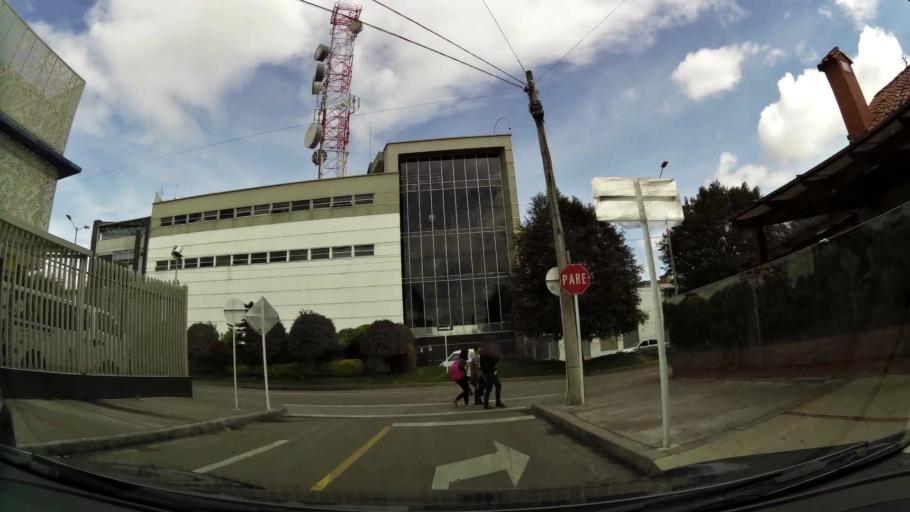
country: CO
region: Bogota D.C.
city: Barrio San Luis
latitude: 4.6853
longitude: -74.0618
